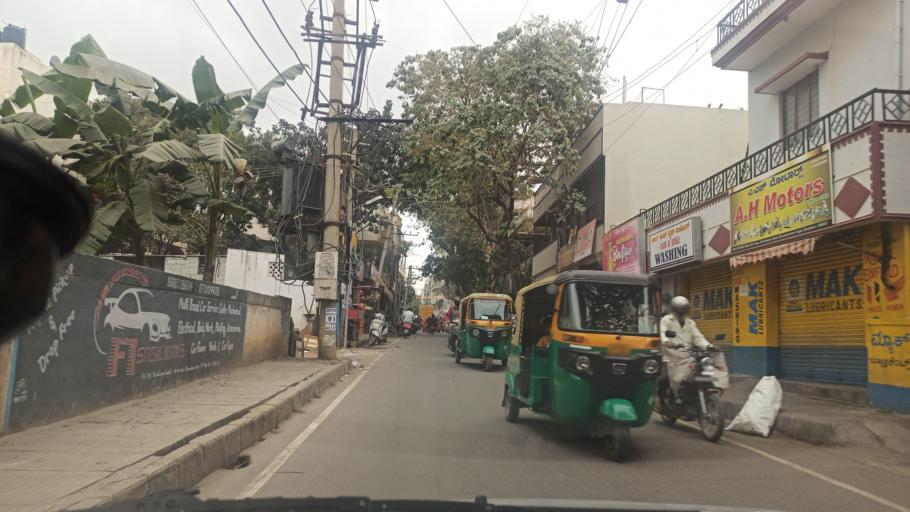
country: IN
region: Karnataka
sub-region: Bangalore Urban
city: Bangalore
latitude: 13.0348
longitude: 77.6036
